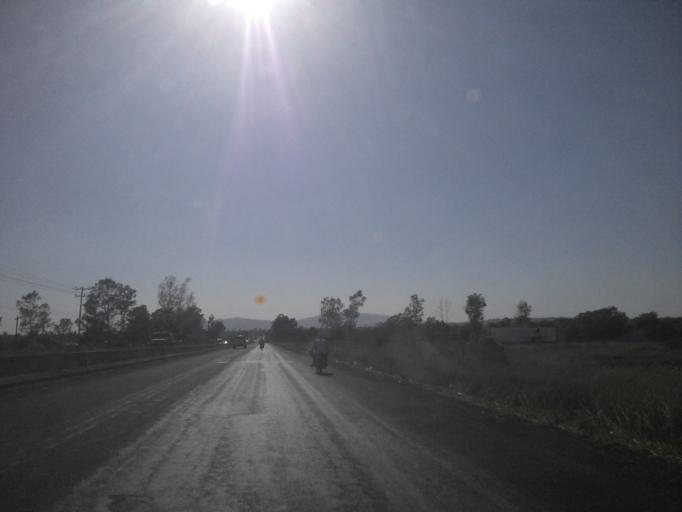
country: MX
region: Jalisco
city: Arandas
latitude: 20.7102
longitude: -102.4016
